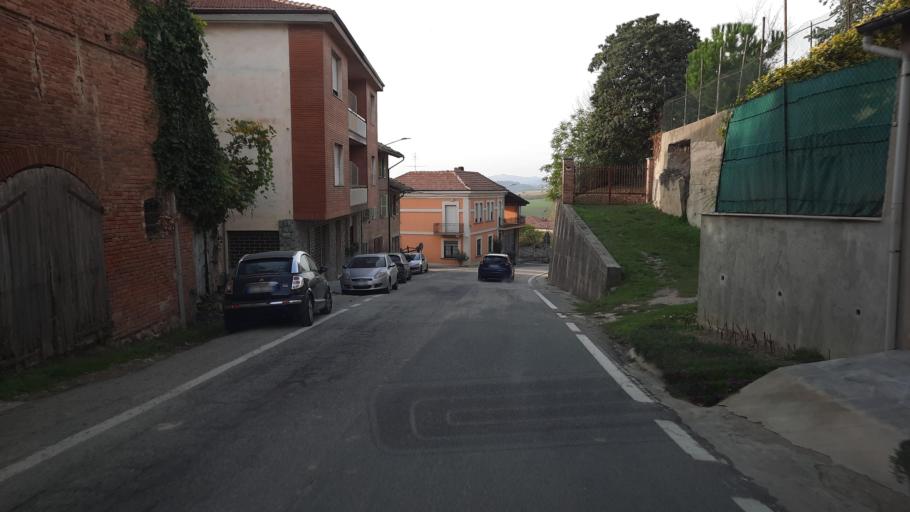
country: IT
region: Piedmont
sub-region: Provincia di Asti
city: Tonco
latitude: 45.0228
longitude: 8.1883
